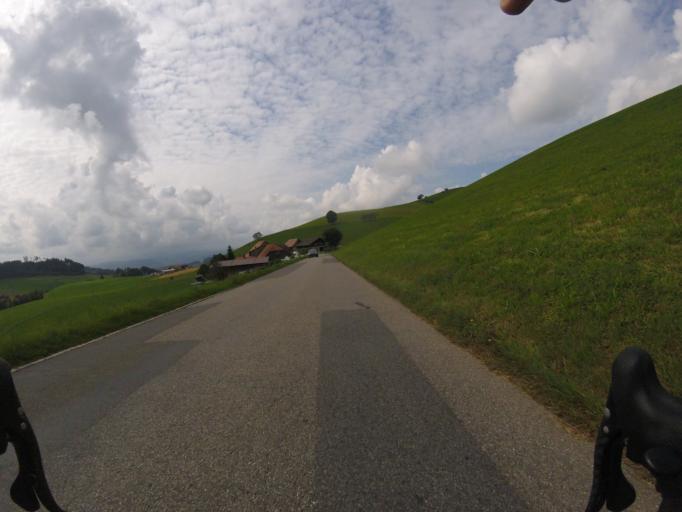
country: CH
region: Bern
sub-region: Bern-Mittelland District
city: Vechigen
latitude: 46.9707
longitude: 7.5772
